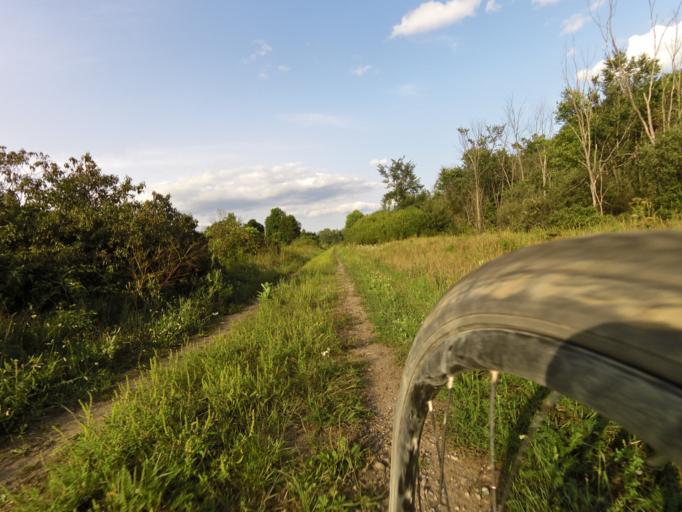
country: CA
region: Ontario
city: Kingston
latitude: 44.4980
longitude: -76.4446
